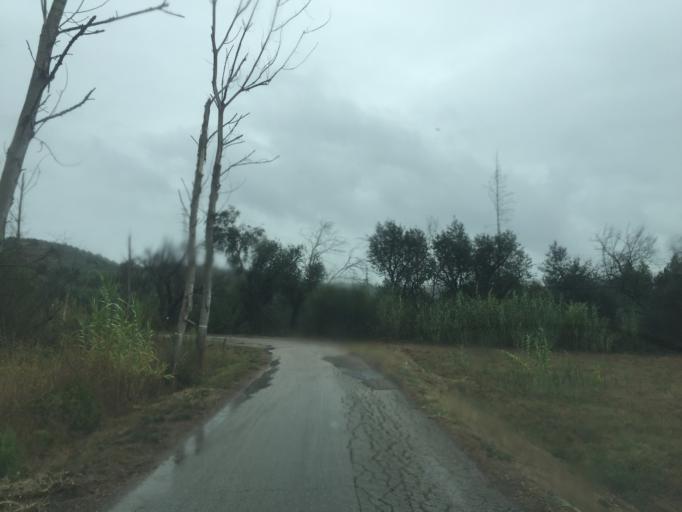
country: PT
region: Coimbra
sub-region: Figueira da Foz
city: Lavos
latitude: 40.0846
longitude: -8.8015
